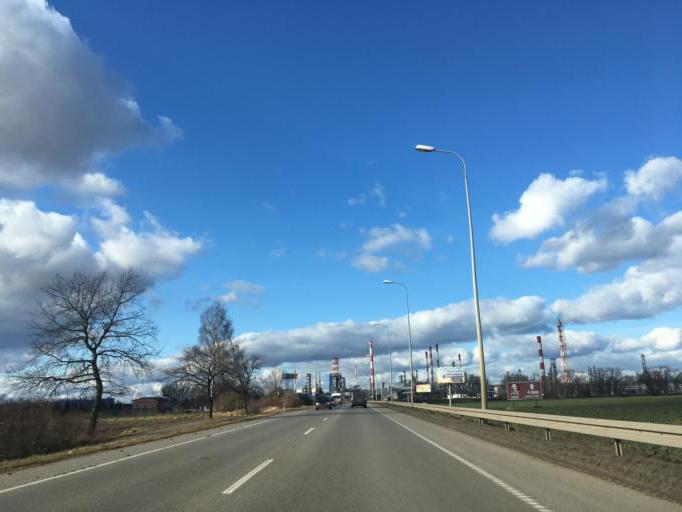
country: PL
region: Pomeranian Voivodeship
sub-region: Gdansk
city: Gdansk
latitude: 54.3343
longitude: 18.7425
